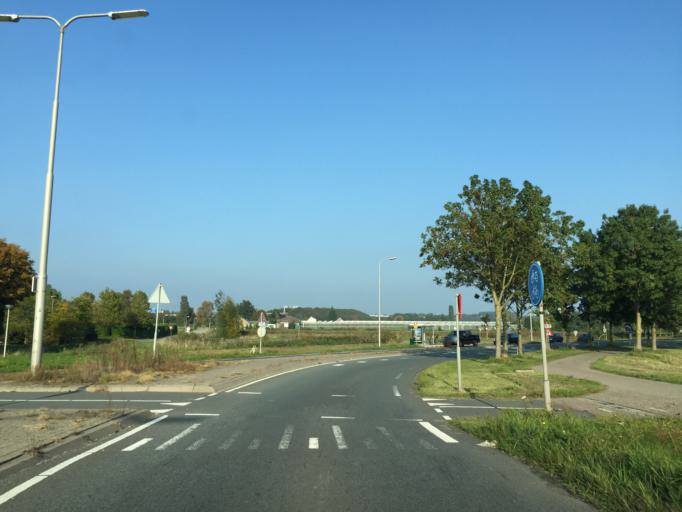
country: NL
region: South Holland
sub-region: Gemeente Barendrecht
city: Barendrecht
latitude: 51.8657
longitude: 4.5575
